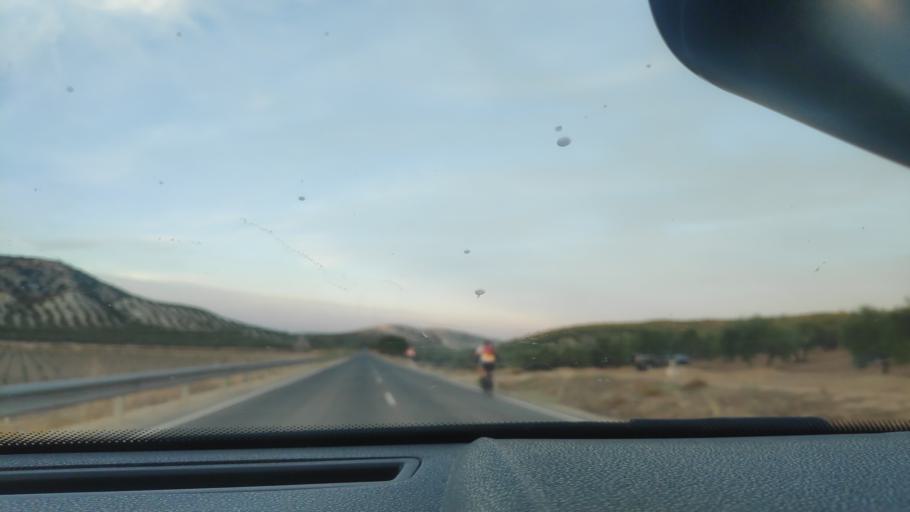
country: ES
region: Andalusia
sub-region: Provincia de Jaen
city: Escanuela
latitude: 37.8635
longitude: -4.0399
